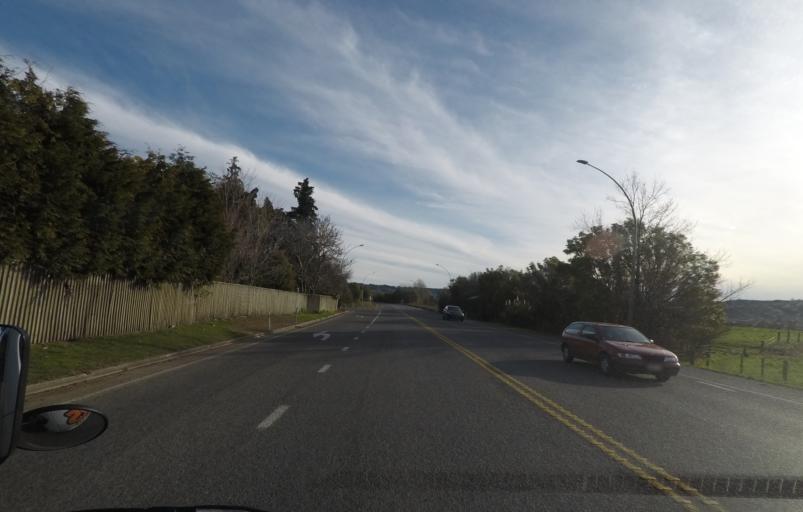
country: NZ
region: Tasman
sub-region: Tasman District
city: Brightwater
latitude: -41.3777
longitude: 173.1007
